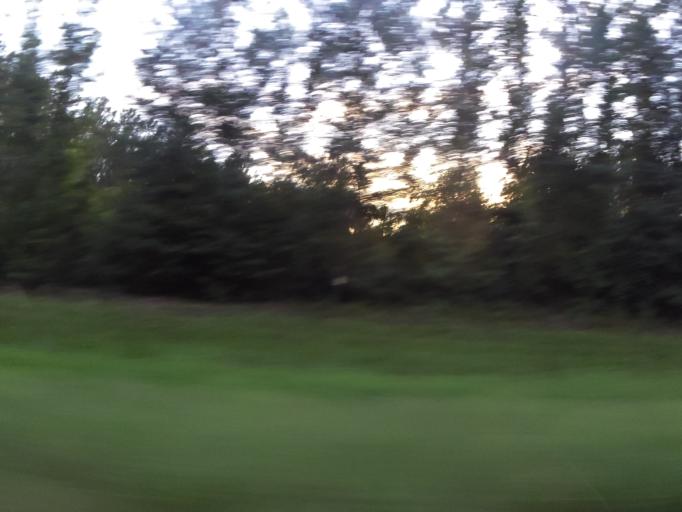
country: US
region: Georgia
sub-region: Camden County
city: Woodbine
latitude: 30.9219
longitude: -81.7143
